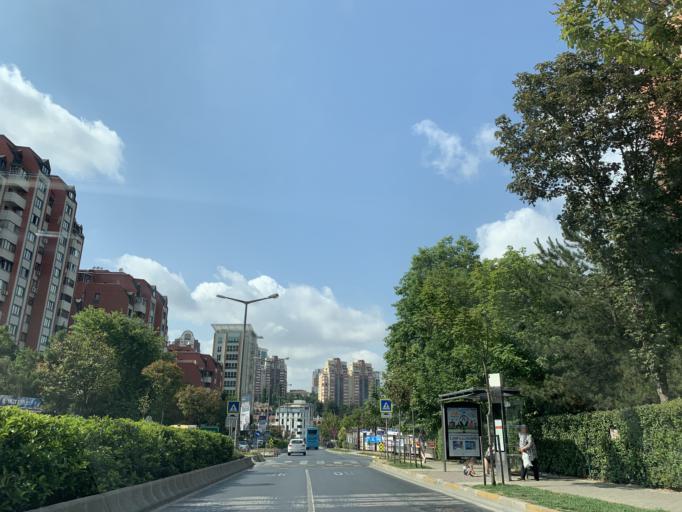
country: TR
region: Istanbul
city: Esenyurt
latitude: 41.0670
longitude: 28.6846
